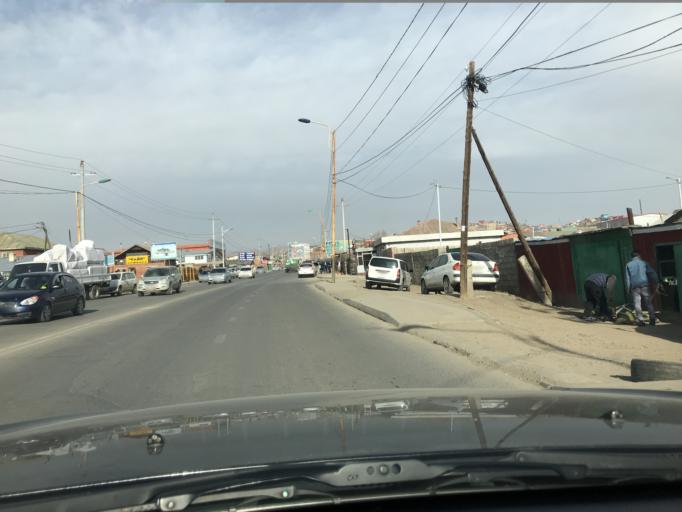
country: MN
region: Ulaanbaatar
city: Ulaanbaatar
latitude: 47.9309
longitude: 106.8882
